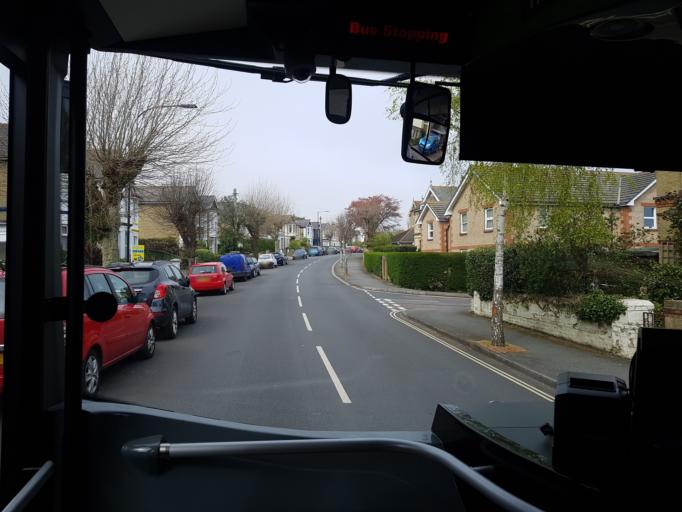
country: GB
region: England
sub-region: Isle of Wight
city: Shanklin
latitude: 50.6340
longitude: -1.1778
